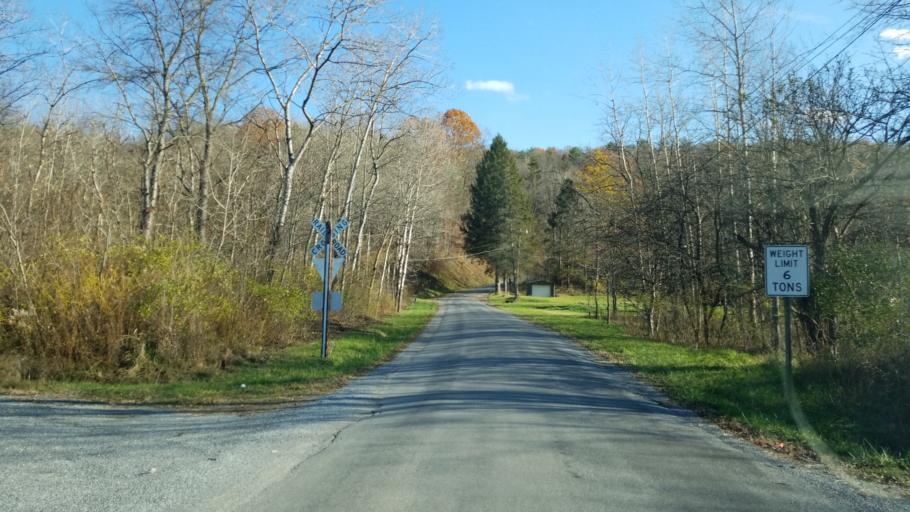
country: US
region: Pennsylvania
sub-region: Clearfield County
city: Treasure Lake
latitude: 41.1535
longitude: -78.6666
